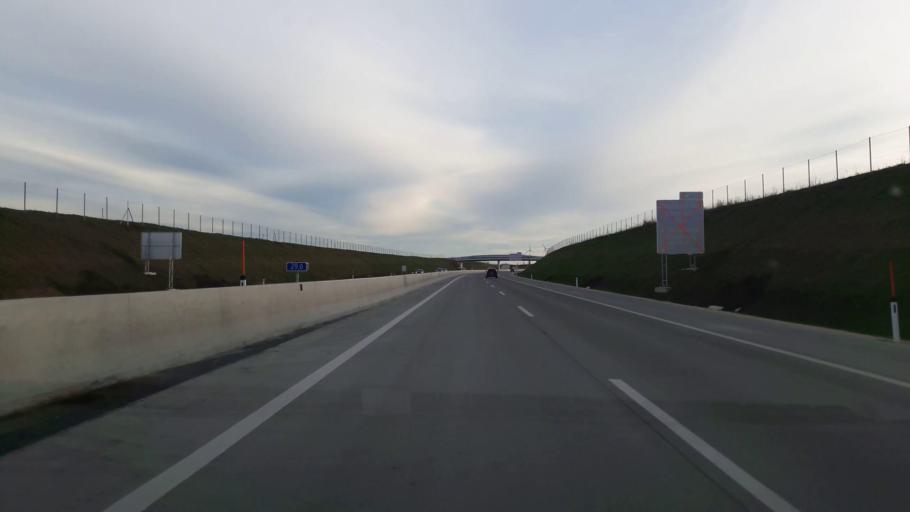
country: AT
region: Lower Austria
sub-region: Politischer Bezirk Mistelbach
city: Wilfersdorf
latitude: 48.5697
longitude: 16.6298
